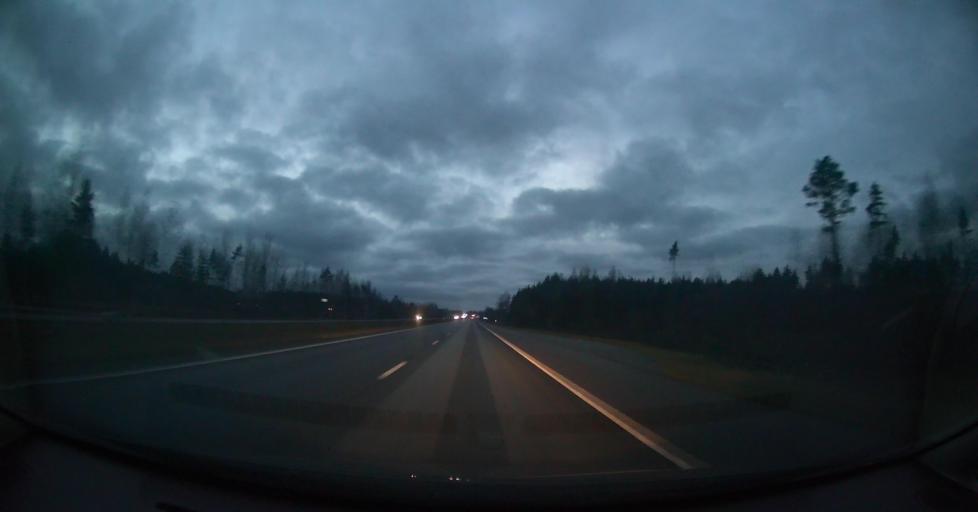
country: EE
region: Harju
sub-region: Kuusalu vald
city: Kuusalu
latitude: 59.4508
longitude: 25.4681
